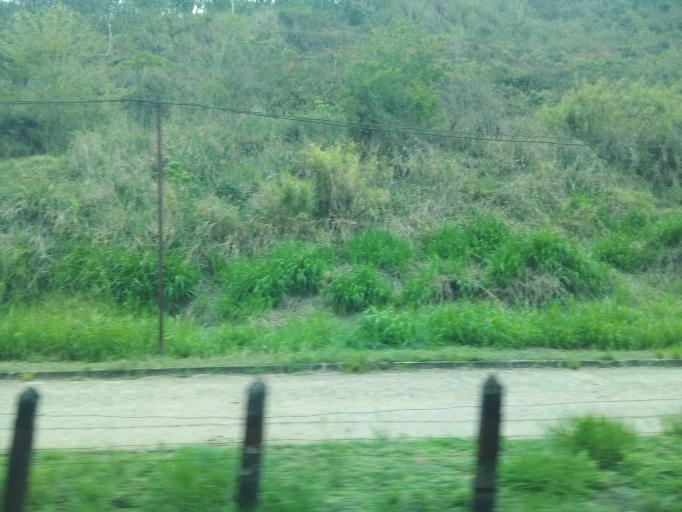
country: BR
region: Minas Gerais
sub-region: Nova Era
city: Nova Era
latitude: -19.7274
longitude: -42.9953
